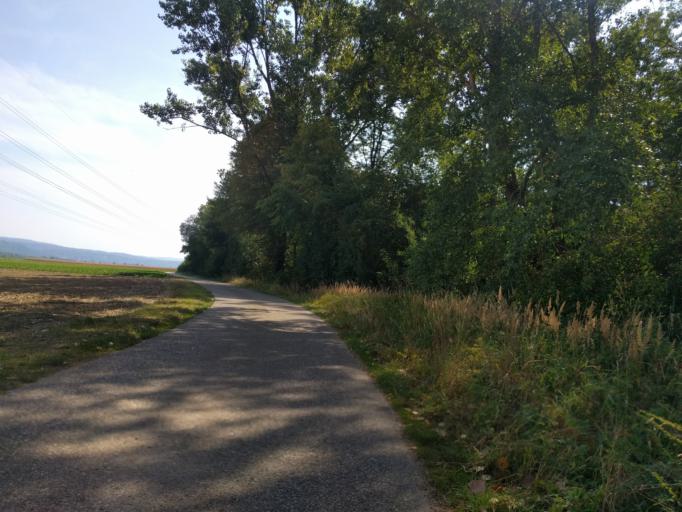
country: DE
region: Bavaria
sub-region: Upper Palatinate
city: Neutraubling
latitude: 48.9949
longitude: 12.2412
